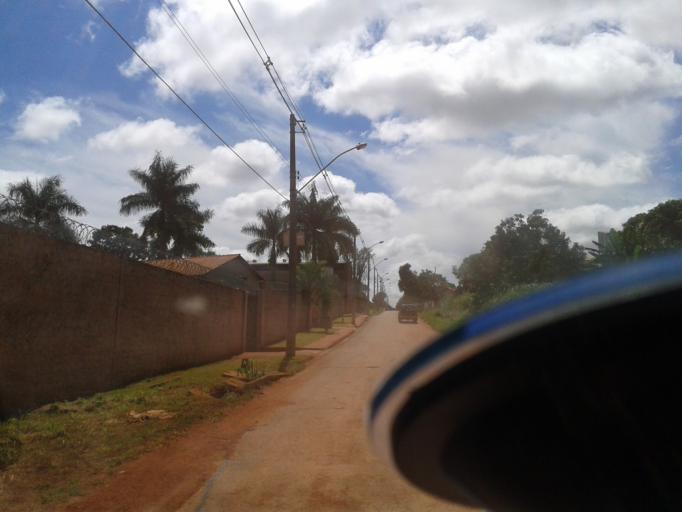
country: BR
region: Goias
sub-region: Goiania
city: Goiania
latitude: -16.6496
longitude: -49.3539
